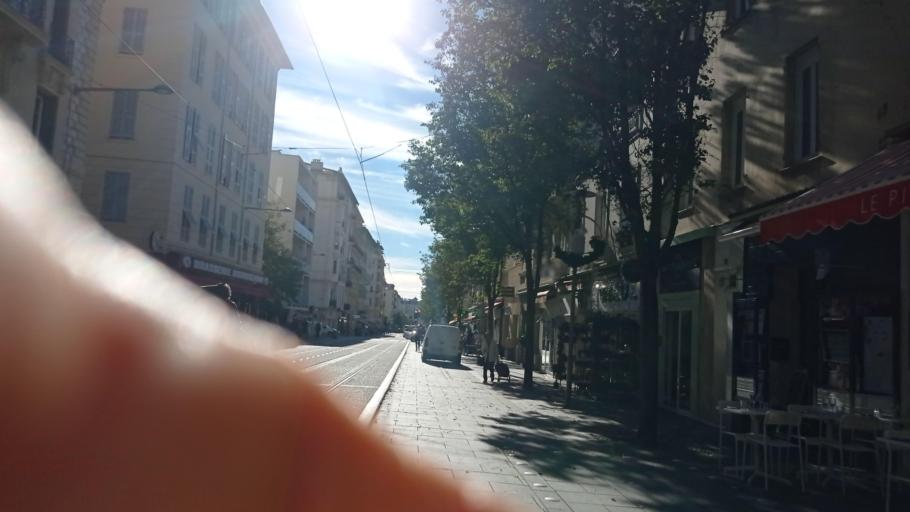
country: FR
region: Provence-Alpes-Cote d'Azur
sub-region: Departement des Alpes-Maritimes
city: Nice
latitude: 43.7138
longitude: 7.2616
